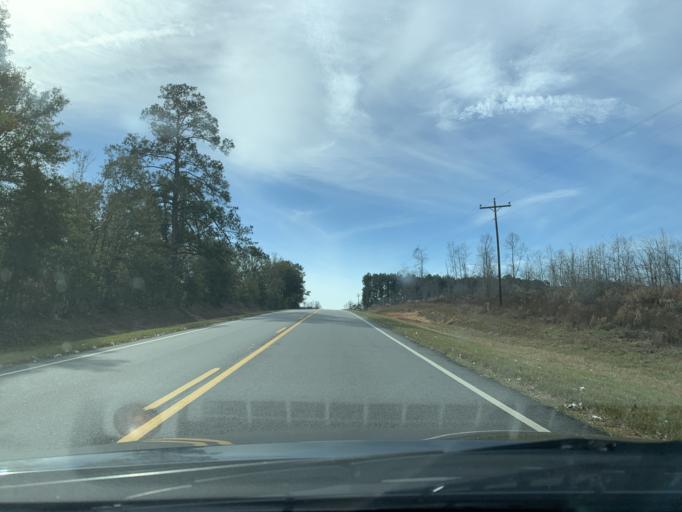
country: US
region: Georgia
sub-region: Turner County
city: Ashburn
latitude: 31.7493
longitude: -83.5610
